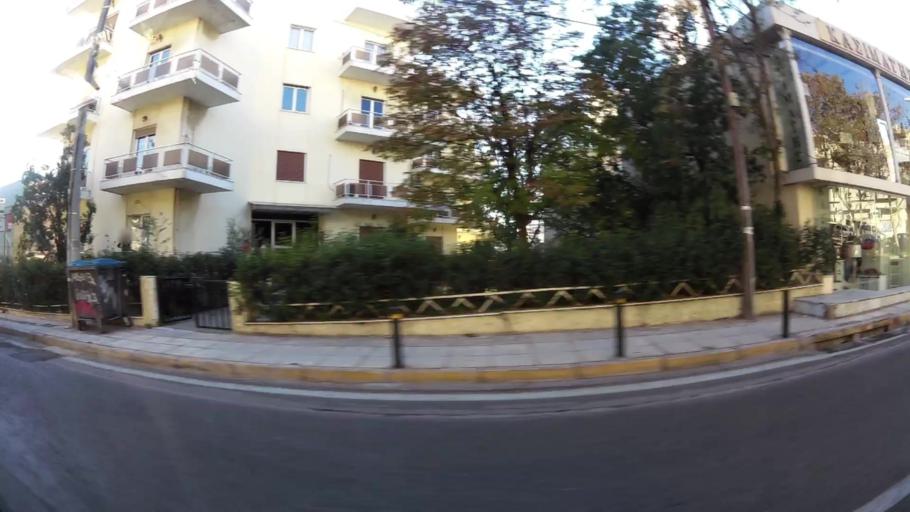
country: GR
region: Attica
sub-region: Nomarchia Athinas
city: Kifisia
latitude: 38.0696
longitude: 23.8110
